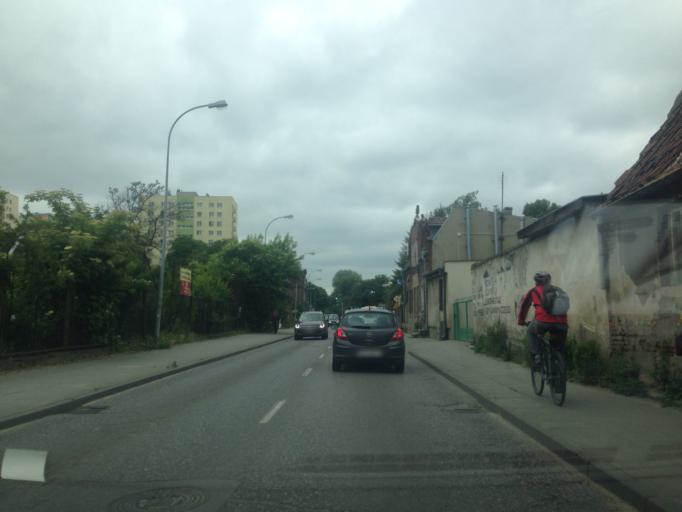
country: PL
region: Pomeranian Voivodeship
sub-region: Gdansk
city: Gdansk
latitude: 54.3302
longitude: 18.6298
